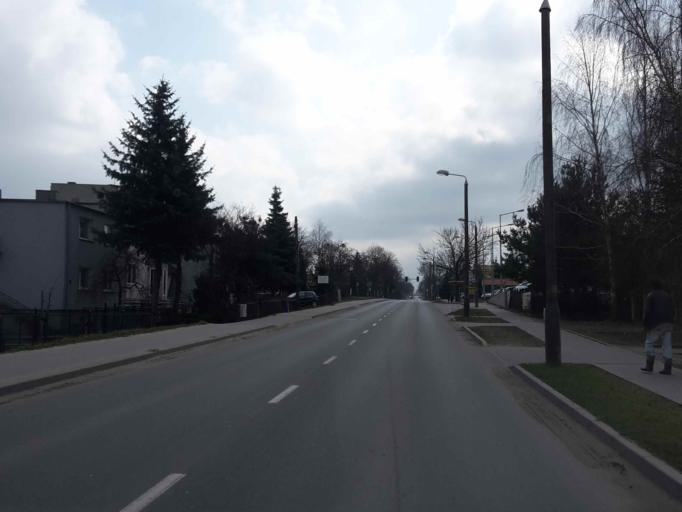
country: PL
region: Kujawsko-Pomorskie
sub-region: Powiat brodnicki
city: Brodnica
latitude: 53.2456
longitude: 19.4048
